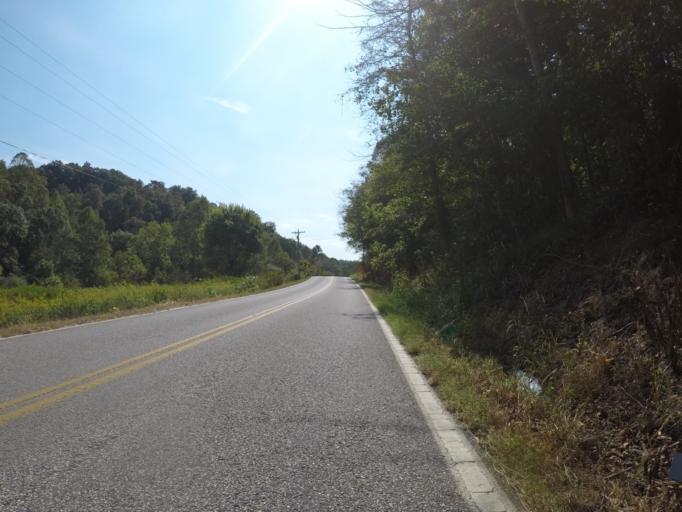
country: US
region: West Virginia
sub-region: Cabell County
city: Lesage
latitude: 38.5652
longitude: -82.3971
